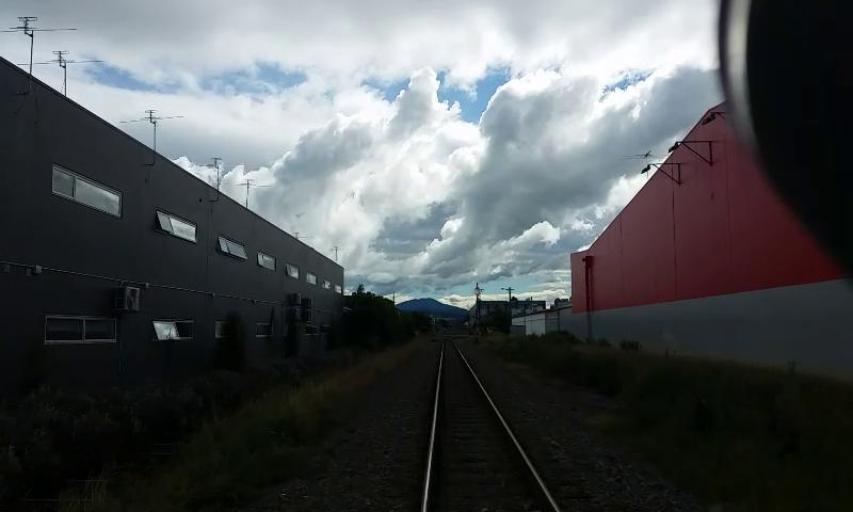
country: NZ
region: Canterbury
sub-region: Waimakariri District
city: Woodend
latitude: -43.3046
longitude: 172.5986
